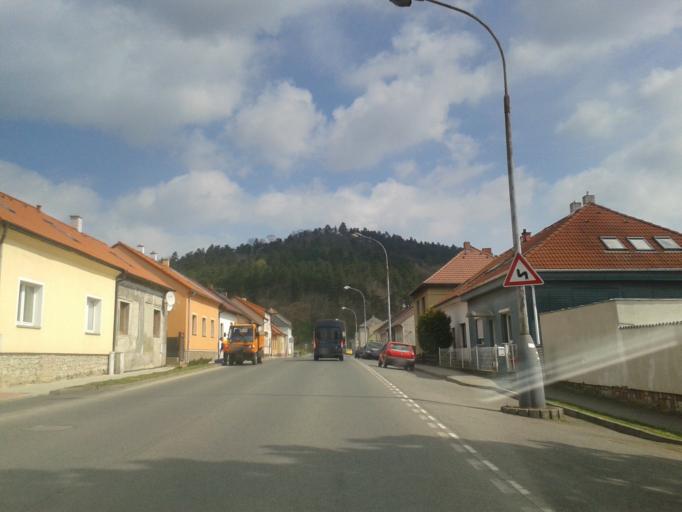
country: CZ
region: Central Bohemia
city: Zdice
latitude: 49.9149
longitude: 13.9819
